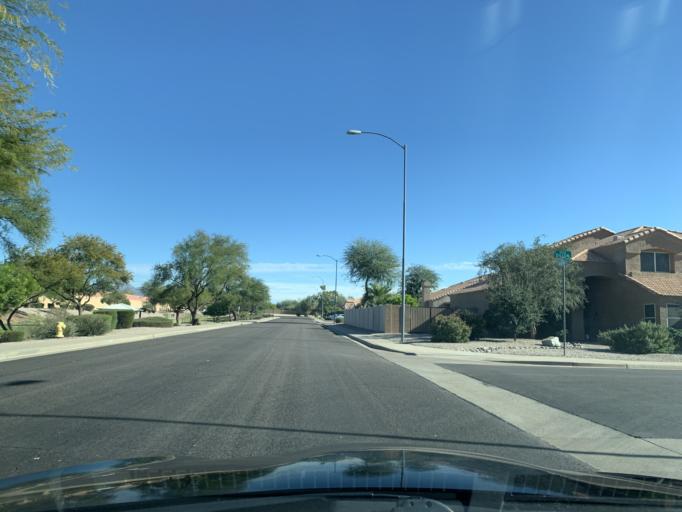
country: US
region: Arizona
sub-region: Pinal County
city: Apache Junction
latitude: 33.3856
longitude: -111.6266
